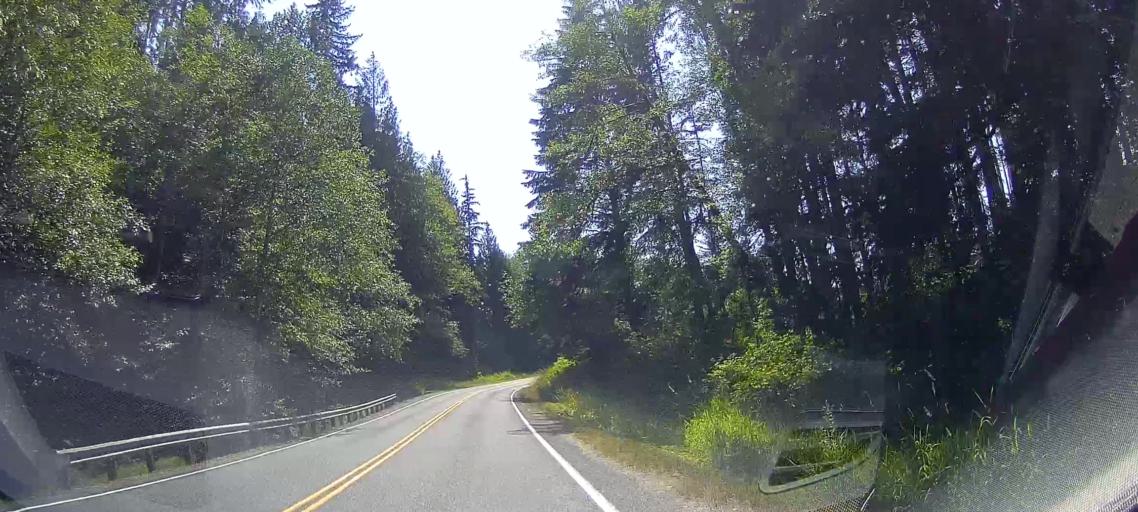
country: US
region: Washington
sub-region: Snohomish County
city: Bryant
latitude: 48.3403
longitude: -122.1098
